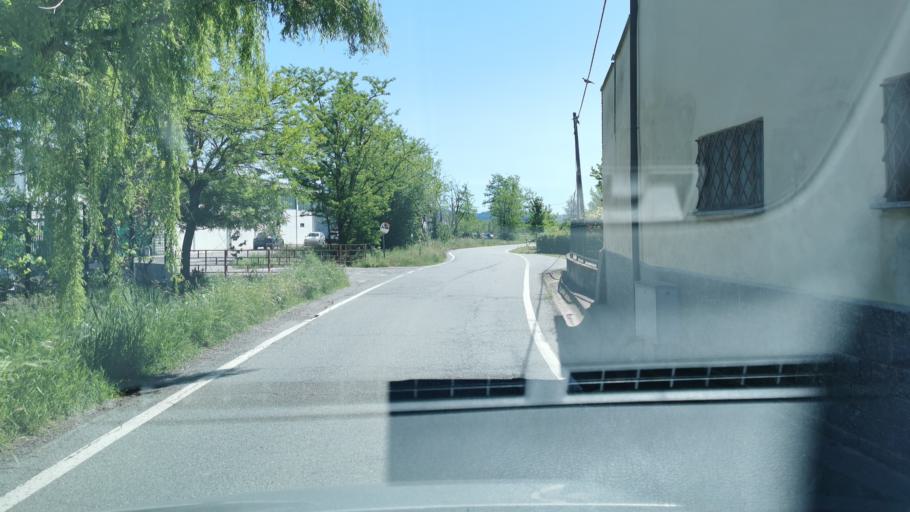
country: IT
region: Piedmont
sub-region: Provincia di Torino
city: Leini
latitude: 45.1692
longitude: 7.7391
